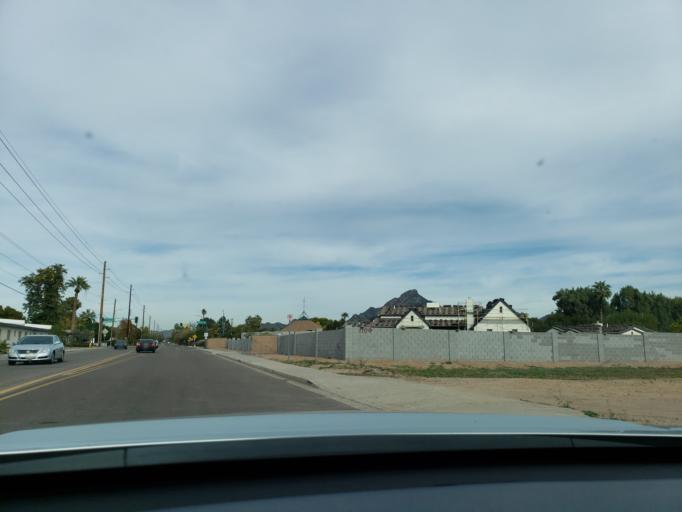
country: US
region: Arizona
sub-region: Maricopa County
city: Phoenix
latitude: 33.5154
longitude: -112.0389
